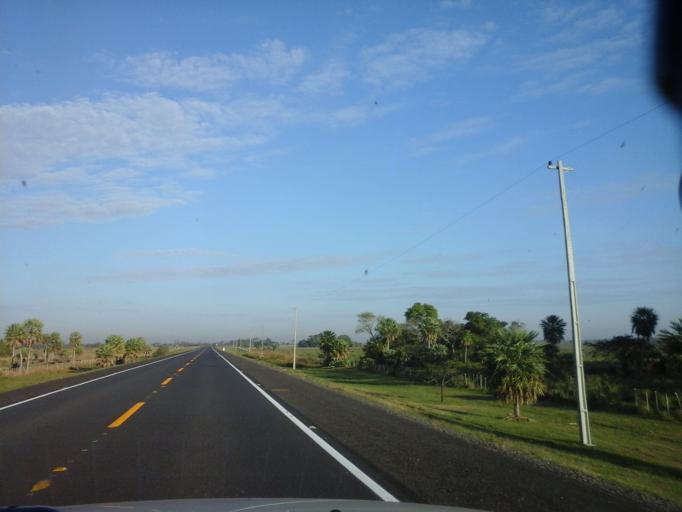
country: PY
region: Neembucu
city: Cerrito
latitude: -26.8659
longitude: -57.5672
